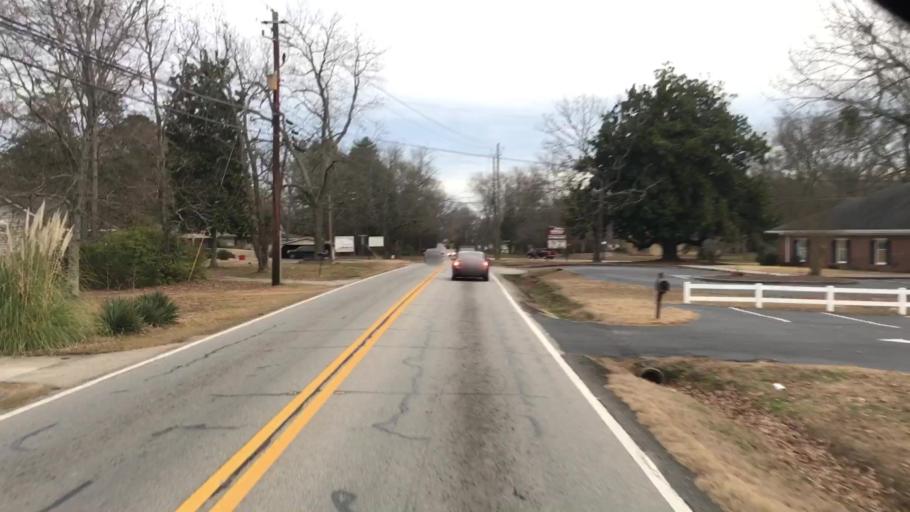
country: US
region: Georgia
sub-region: Barrow County
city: Winder
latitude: 33.9989
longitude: -83.7442
